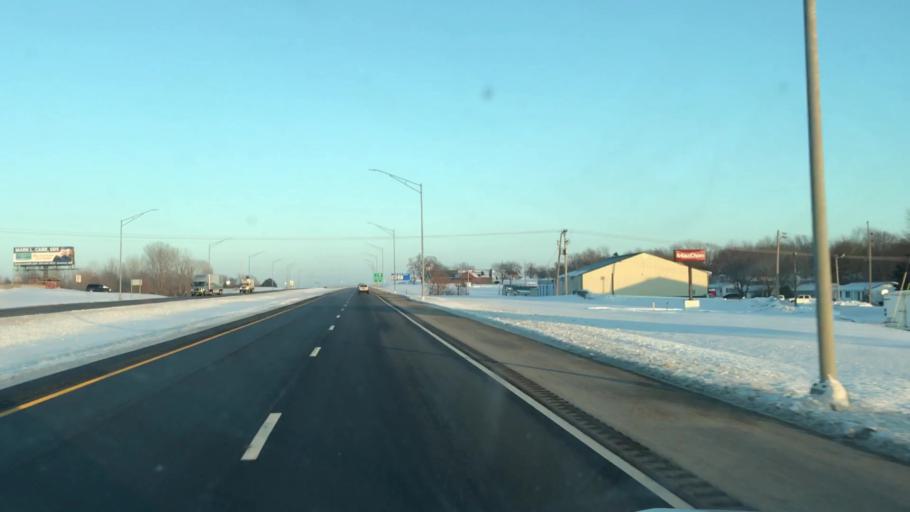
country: US
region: Missouri
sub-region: Clinton County
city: Cameron
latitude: 39.7542
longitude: -94.2448
